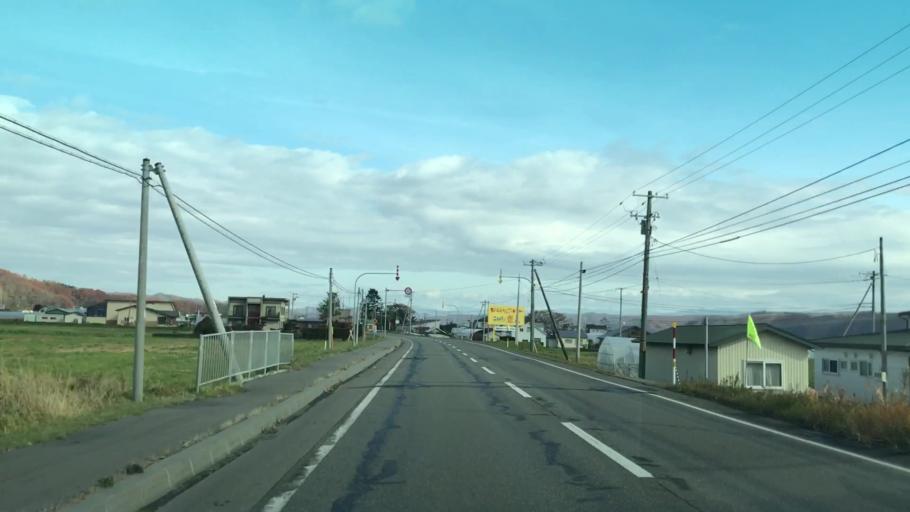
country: JP
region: Hokkaido
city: Shizunai-furukawacho
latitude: 42.5490
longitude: 142.0688
